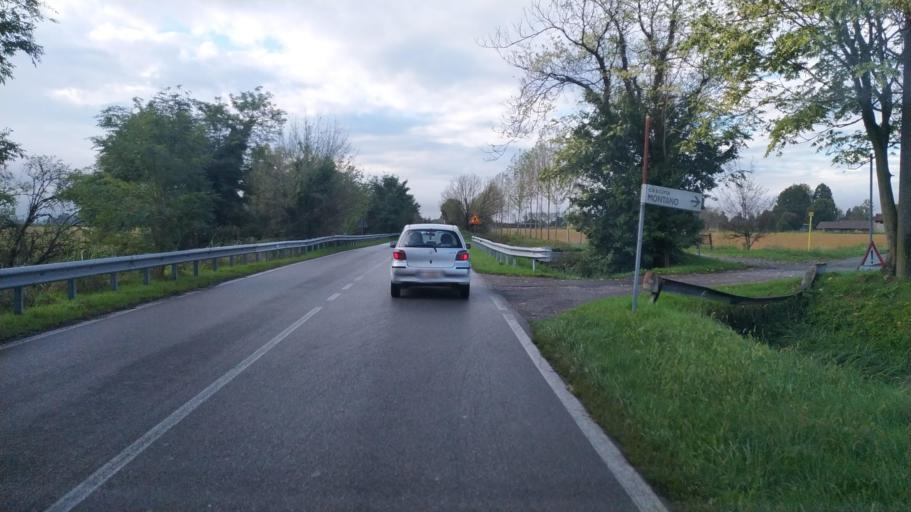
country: IT
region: Lombardy
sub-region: Citta metropolitana di Milano
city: Gaggiano
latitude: 45.3946
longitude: 9.0297
